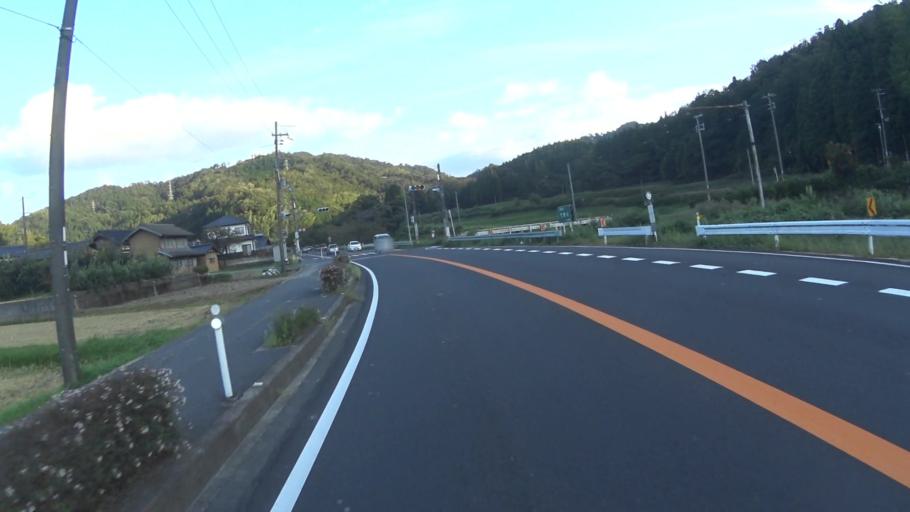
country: JP
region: Kyoto
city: Miyazu
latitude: 35.5640
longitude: 135.0961
